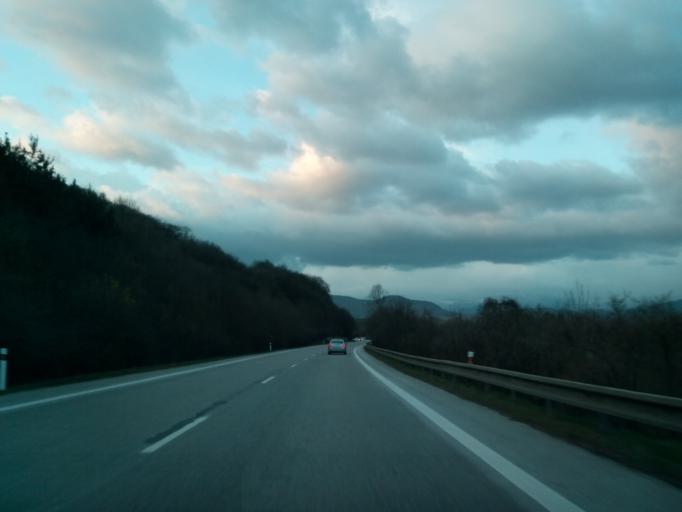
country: SK
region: Kosicky
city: Roznava
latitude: 48.5981
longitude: 20.4730
